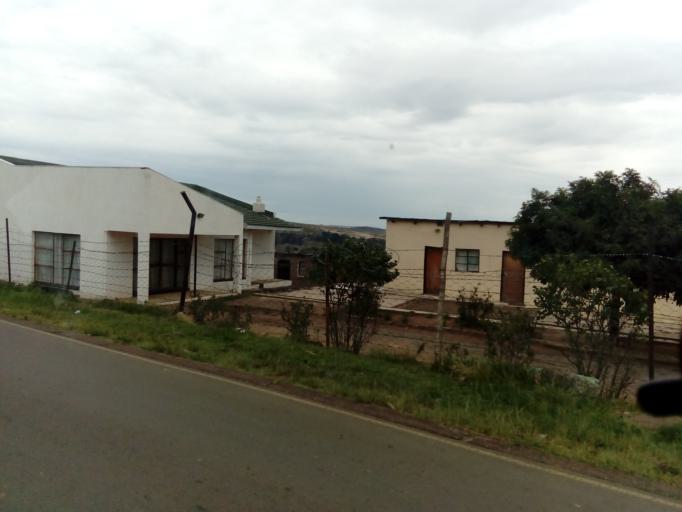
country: LS
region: Berea
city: Teyateyaneng
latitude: -29.1031
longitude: 27.9584
